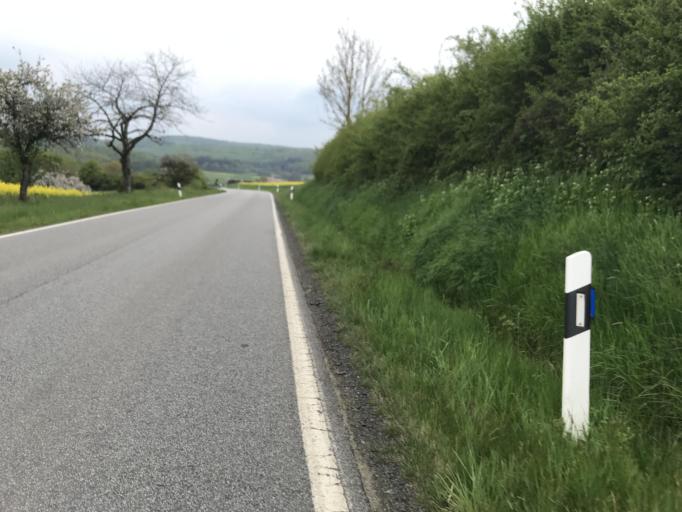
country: DE
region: Hesse
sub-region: Regierungsbezirk Giessen
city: Laubach
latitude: 50.5195
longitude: 9.0141
